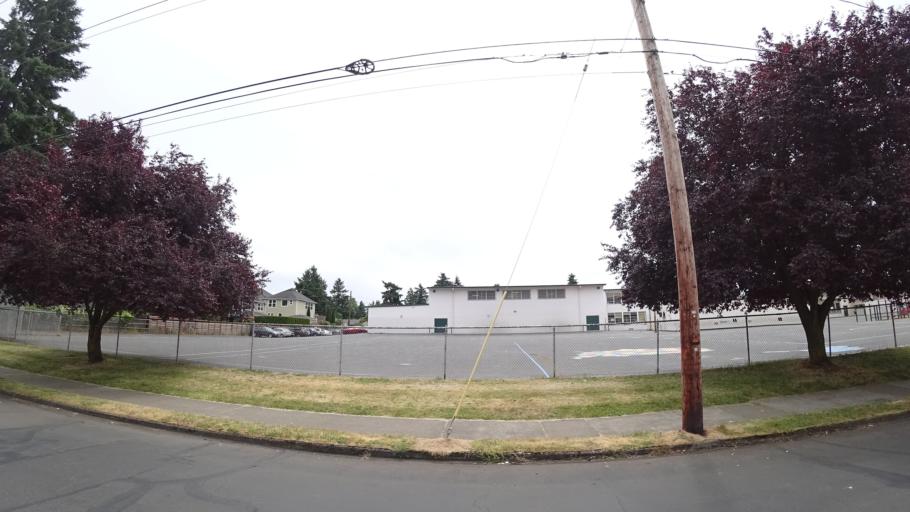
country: US
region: Oregon
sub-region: Multnomah County
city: Portland
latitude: 45.5735
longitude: -122.6908
